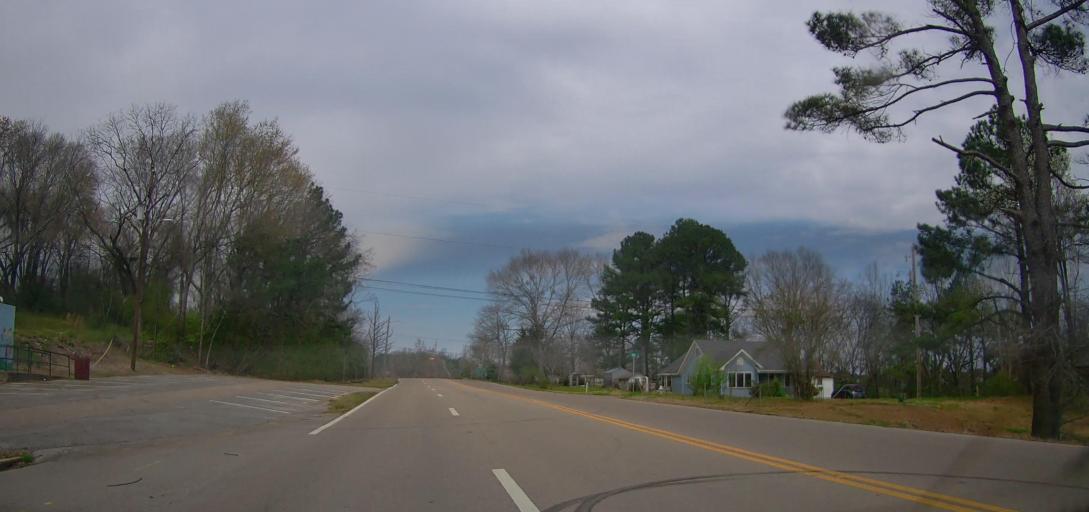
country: US
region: Mississippi
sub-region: Lee County
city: Tupelo
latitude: 34.2693
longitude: -88.7034
